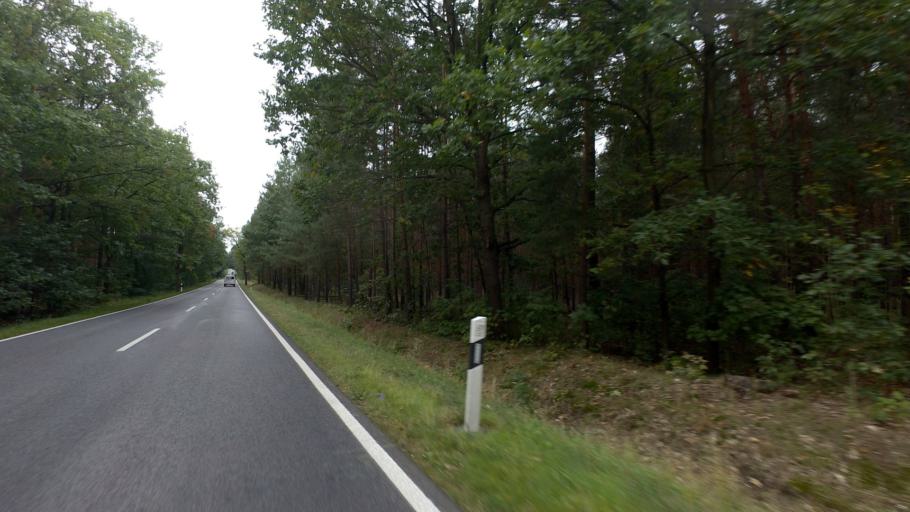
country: DE
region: Brandenburg
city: Baruth
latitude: 52.0346
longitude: 13.4849
